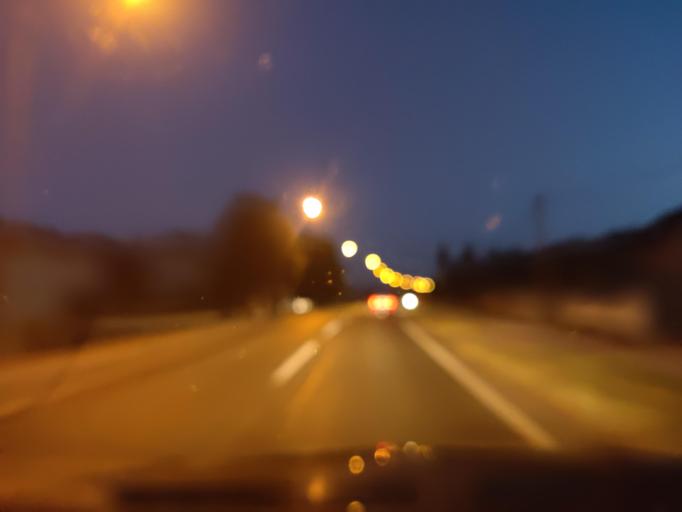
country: HR
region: Medimurska
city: Senkovec
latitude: 46.4108
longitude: 16.4230
